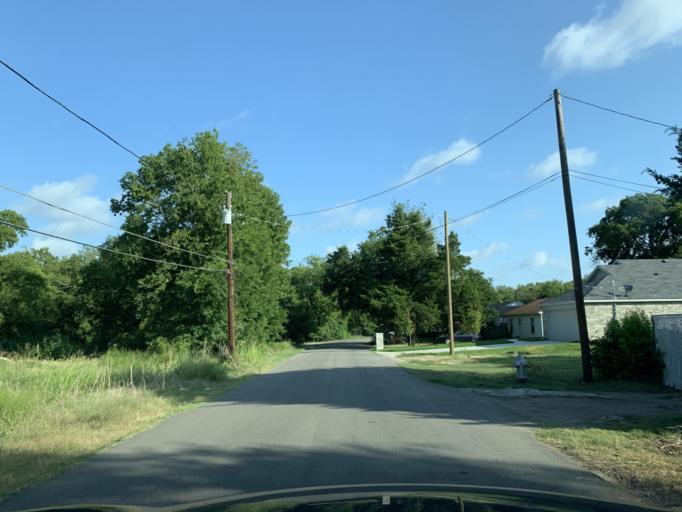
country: US
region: Texas
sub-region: Dallas County
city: Hutchins
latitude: 32.6794
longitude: -96.7673
